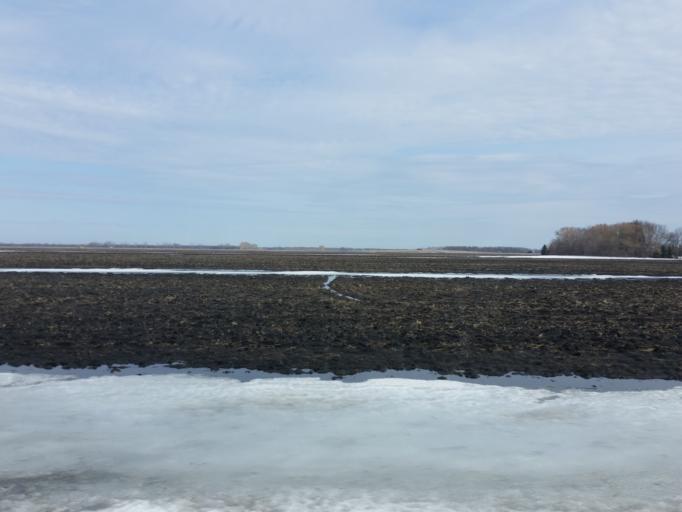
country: US
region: North Dakota
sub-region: Walsh County
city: Grafton
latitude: 48.4145
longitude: -97.2121
